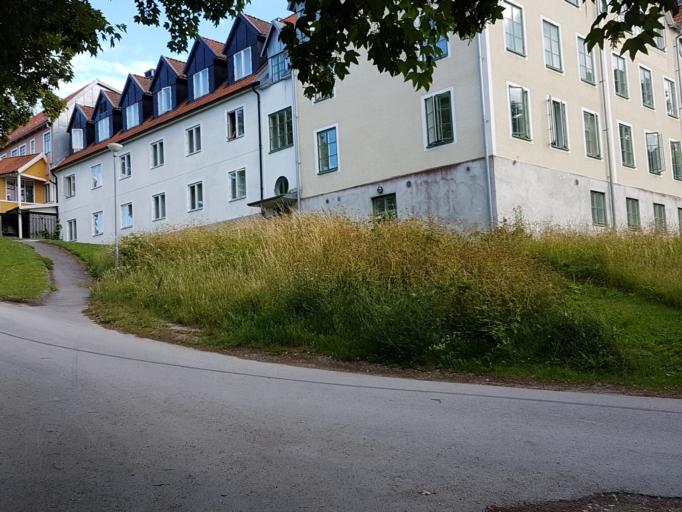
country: SE
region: Gotland
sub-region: Gotland
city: Visby
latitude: 57.6353
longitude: 18.2862
